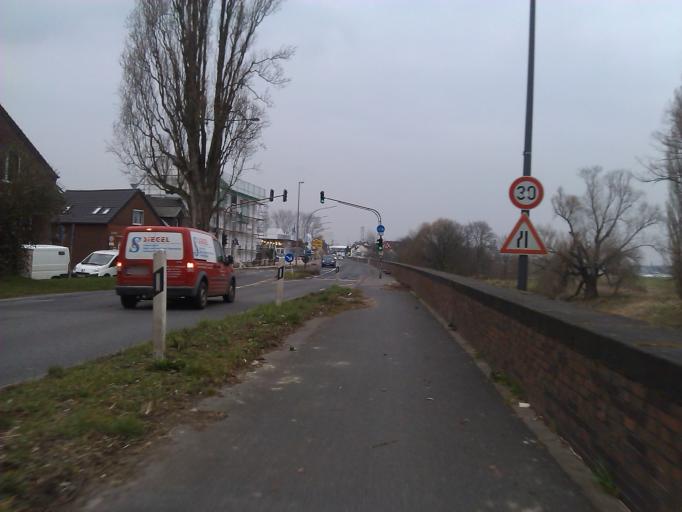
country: DE
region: North Rhine-Westphalia
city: Monheim am Rhein
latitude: 51.0671
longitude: 6.8666
